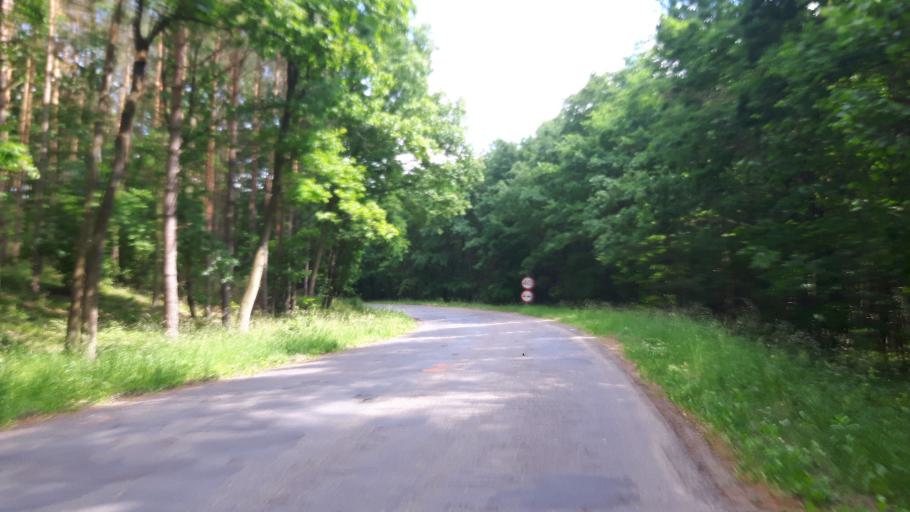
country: PL
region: West Pomeranian Voivodeship
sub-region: Powiat goleniowski
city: Osina
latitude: 53.6729
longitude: 15.0245
